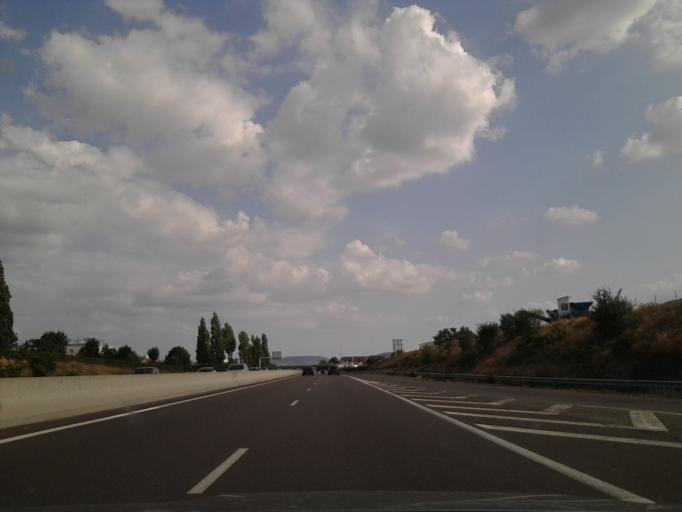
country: FR
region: Auvergne
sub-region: Departement du Puy-de-Dome
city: Perignat-les-Sarlieve
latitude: 45.7584
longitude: 3.1401
